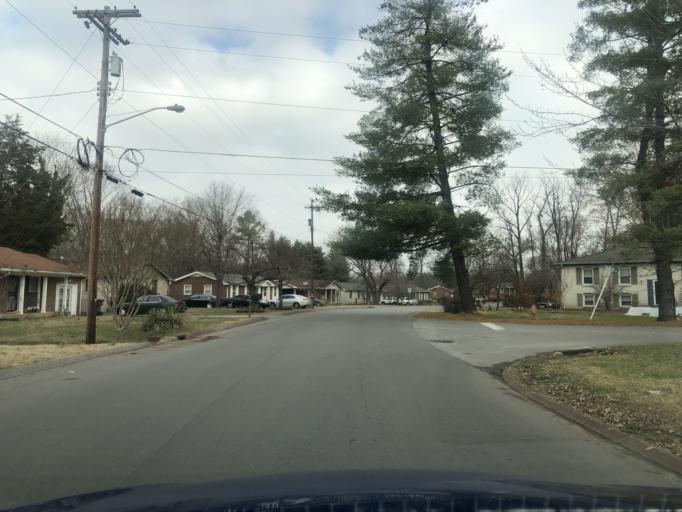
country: US
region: Tennessee
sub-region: Davidson County
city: Oak Hill
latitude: 36.0921
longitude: -86.7173
